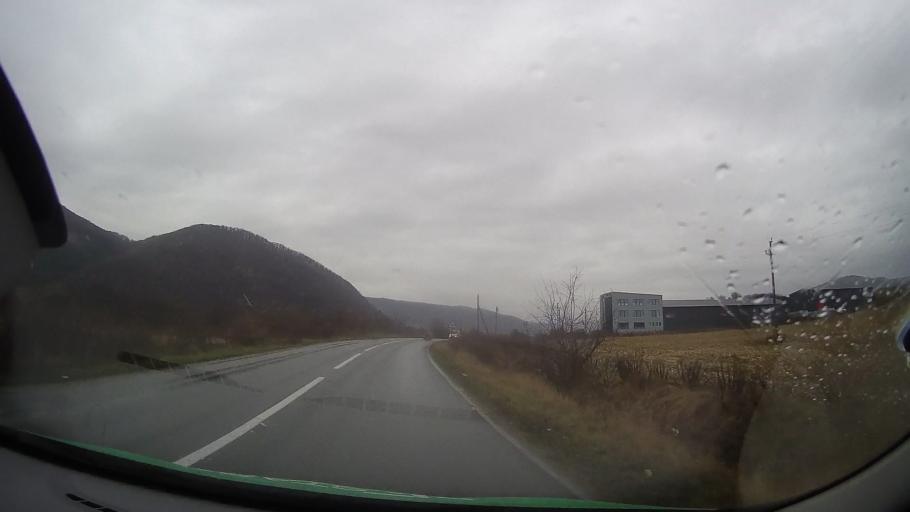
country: RO
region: Bistrita-Nasaud
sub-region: Municipiul Bistrita
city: Viisoara
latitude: 47.0566
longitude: 24.4434
